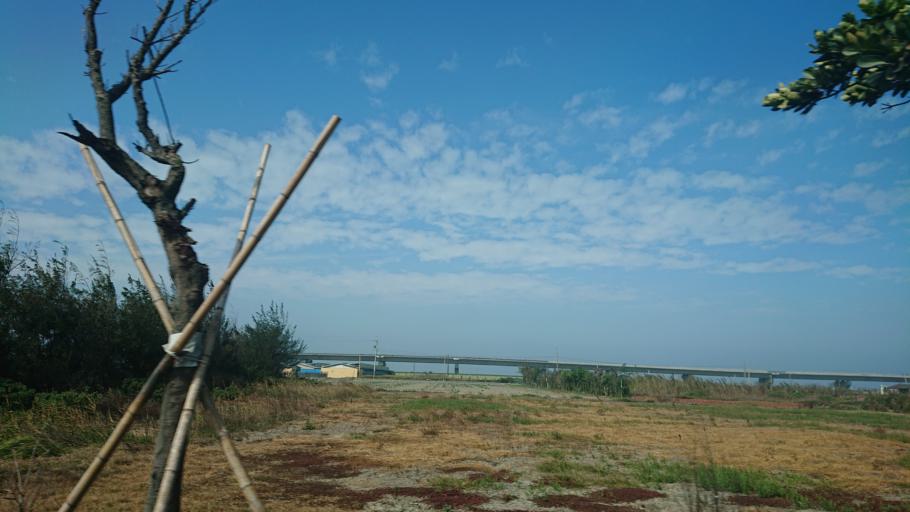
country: TW
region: Taiwan
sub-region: Yunlin
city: Douliu
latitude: 23.8992
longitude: 120.3055
